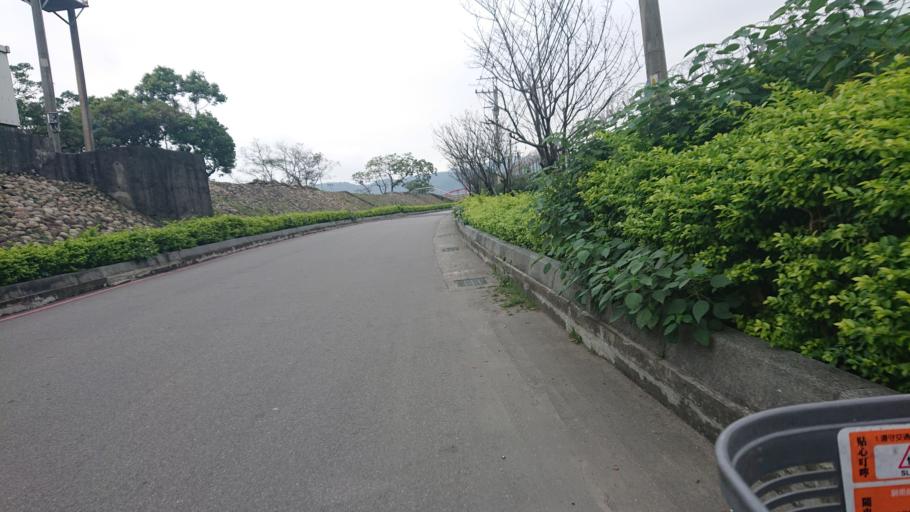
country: TW
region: Taiwan
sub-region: Taoyuan
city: Taoyuan
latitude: 24.9360
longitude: 121.3513
